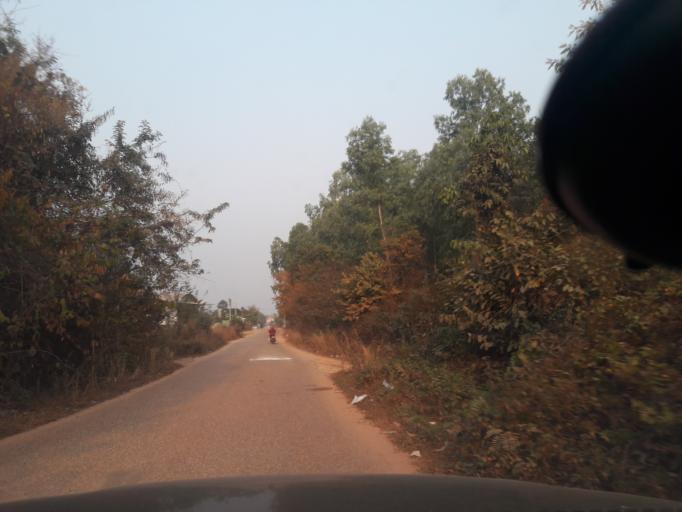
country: LA
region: Vientiane
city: Vientiane
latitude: 18.0634
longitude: 102.5289
